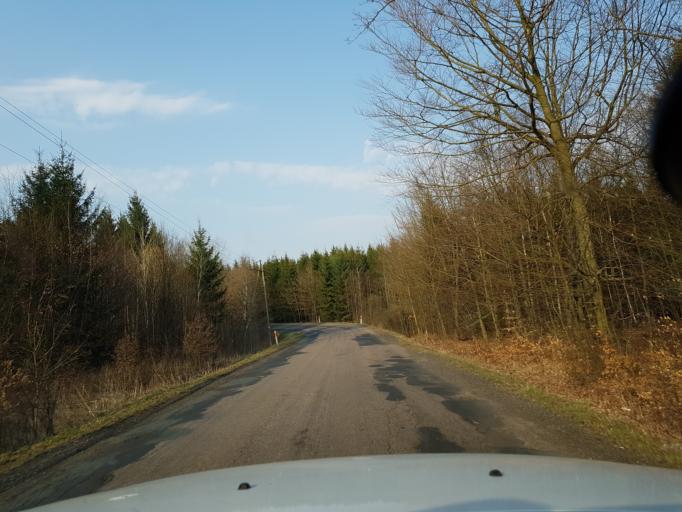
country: PL
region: West Pomeranian Voivodeship
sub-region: Powiat swidwinski
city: Polczyn-Zdroj
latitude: 53.7308
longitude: 16.0744
